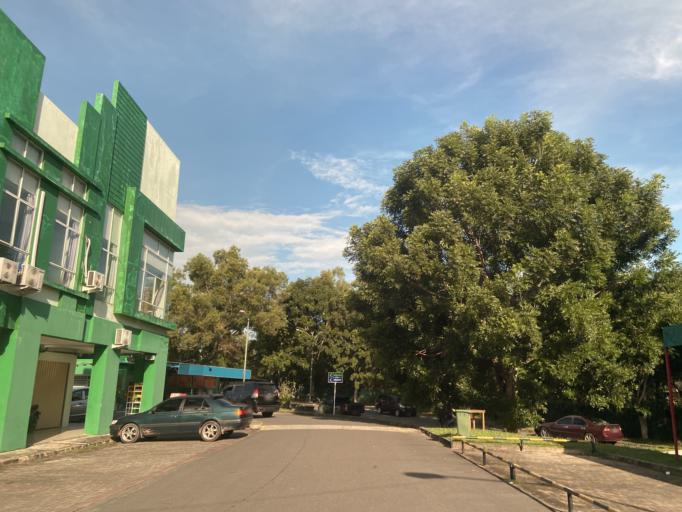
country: SG
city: Singapore
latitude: 1.1057
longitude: 104.0298
